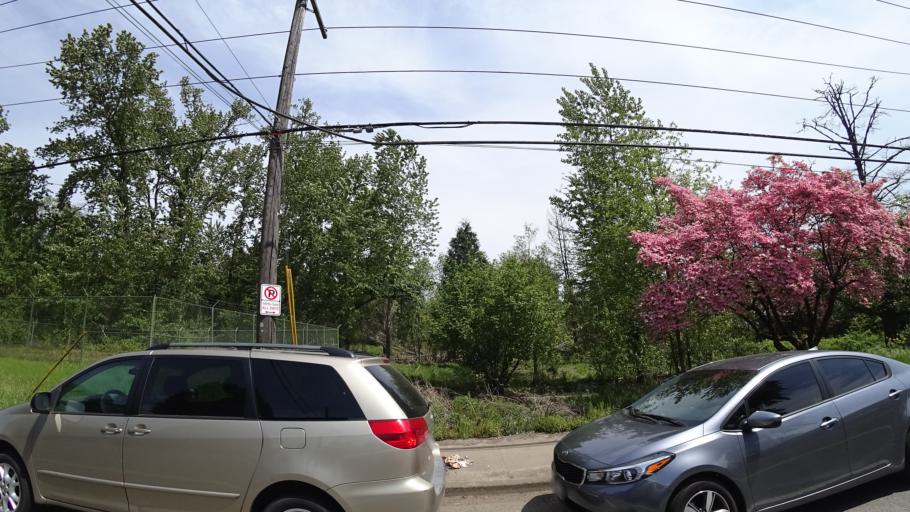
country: US
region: Oregon
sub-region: Clackamas County
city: Milwaukie
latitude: 45.4636
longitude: -122.6158
